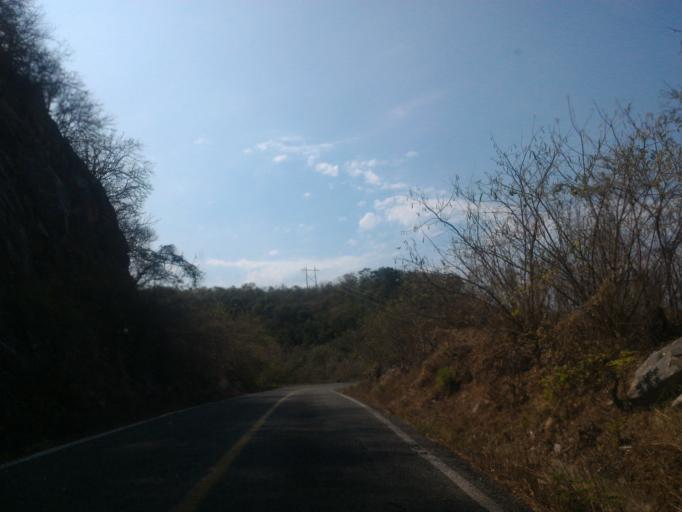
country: MX
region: Michoacan
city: Coahuayana Viejo
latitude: 18.4915
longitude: -103.5731
